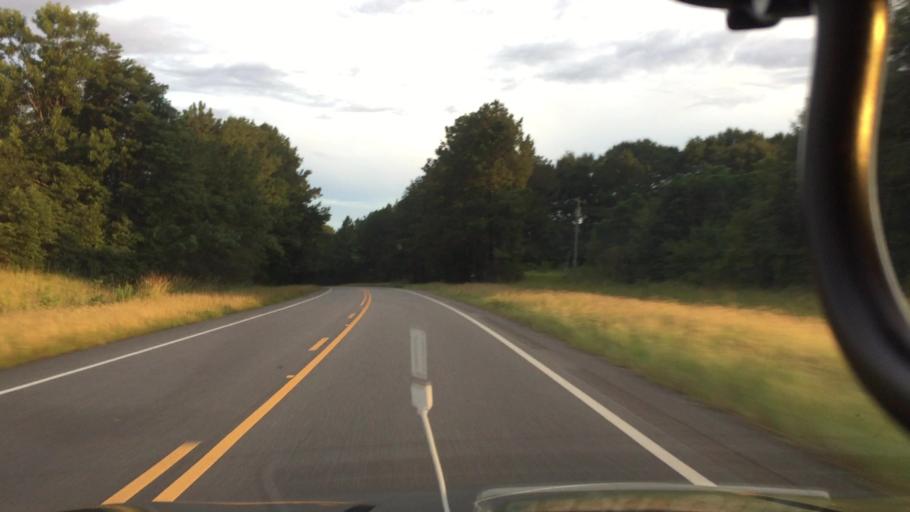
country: US
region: Alabama
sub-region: Pike County
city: Brundidge
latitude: 31.5990
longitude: -85.9469
